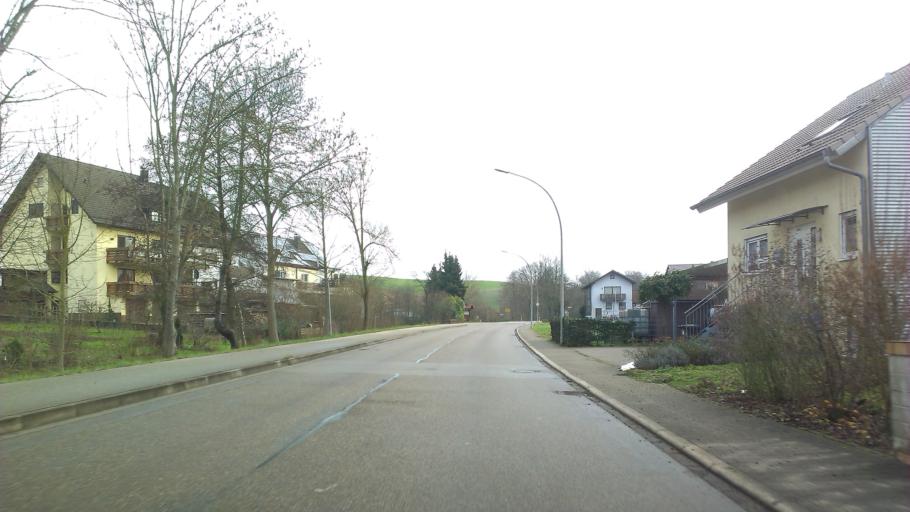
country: DE
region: Baden-Wuerttemberg
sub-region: Karlsruhe Region
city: Balzfeld
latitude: 49.2689
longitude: 8.7912
